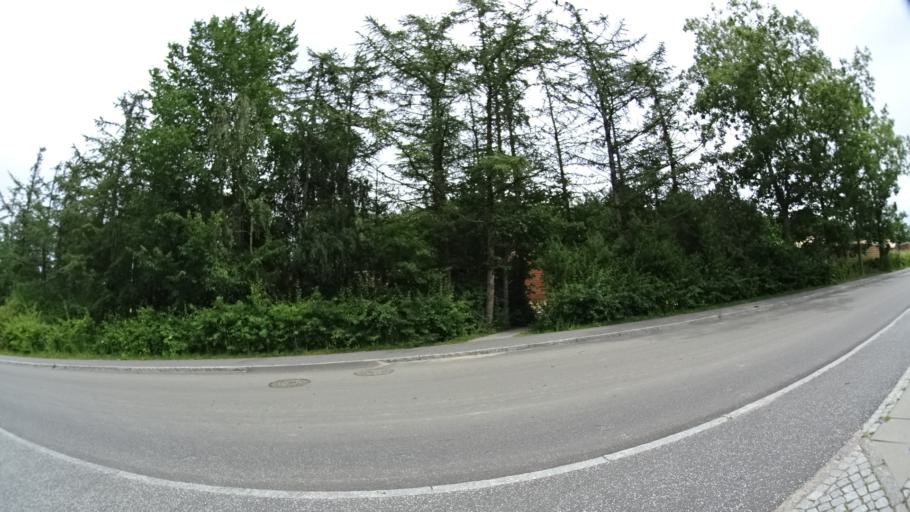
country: DK
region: Central Jutland
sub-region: Arhus Kommune
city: Stavtrup
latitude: 56.1212
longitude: 10.1333
